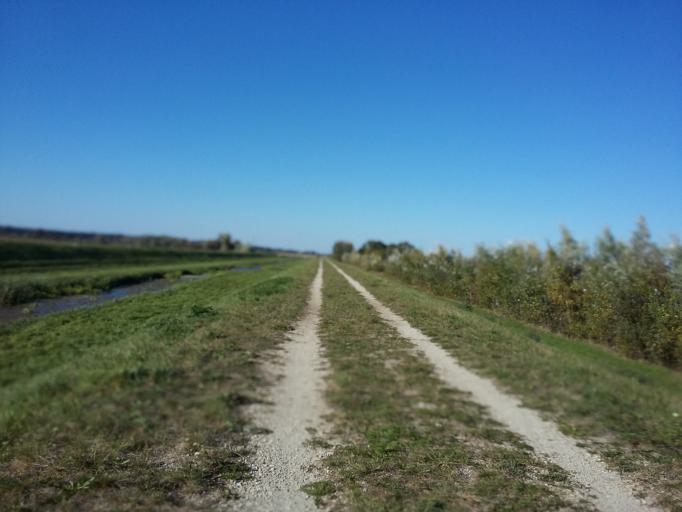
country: SK
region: Bratislavsky
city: Stupava
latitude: 48.3115
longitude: 16.9721
